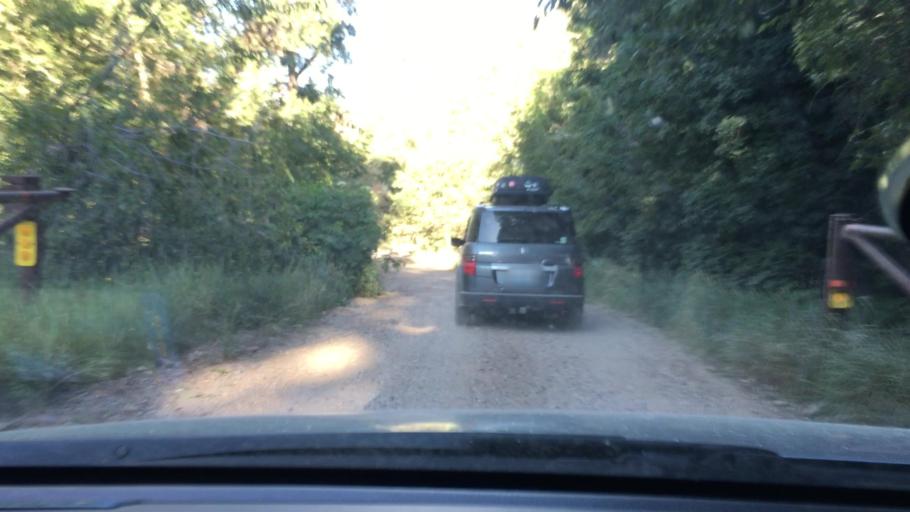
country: US
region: Utah
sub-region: Sanpete County
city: Fountain Green
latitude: 39.5551
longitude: -111.6831
